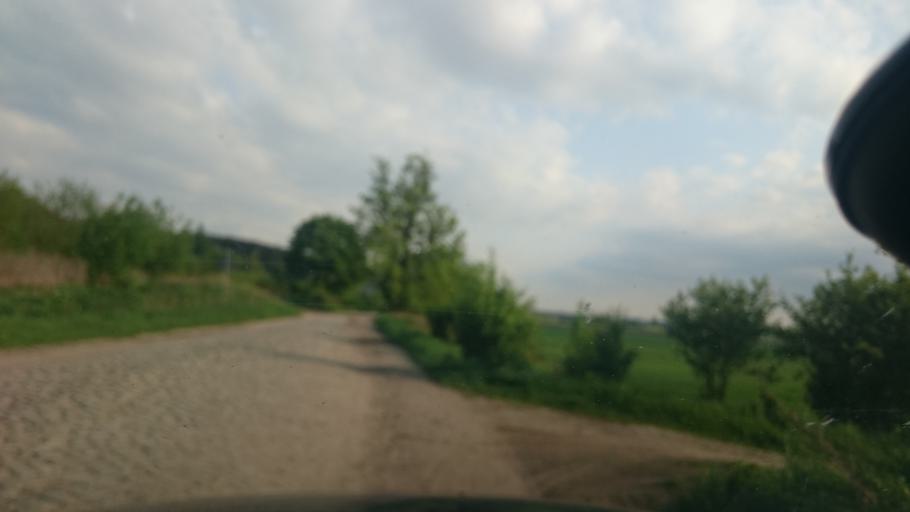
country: PL
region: Kujawsko-Pomorskie
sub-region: Grudziadz
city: Grudziadz
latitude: 53.4781
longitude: 18.8132
